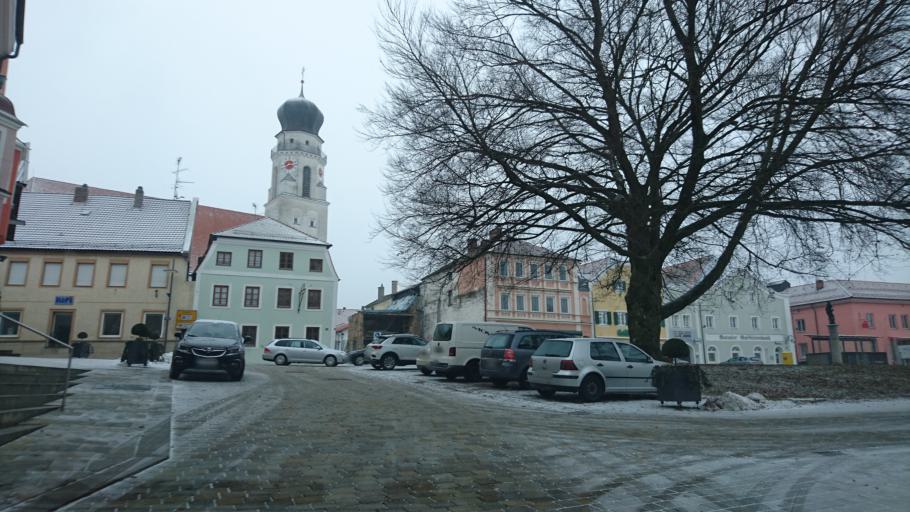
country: DE
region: Bavaria
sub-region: Lower Bavaria
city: Bad Griesbach
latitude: 48.4519
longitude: 13.1926
